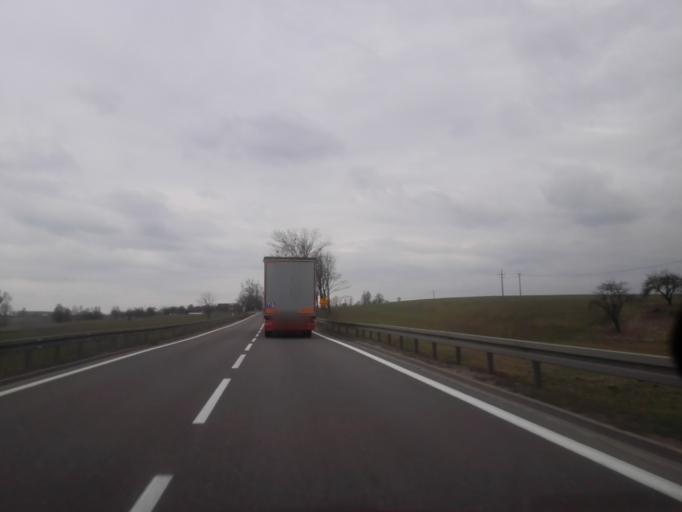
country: PL
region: Podlasie
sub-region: Powiat augustowski
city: Augustow
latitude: 53.7955
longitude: 22.8750
